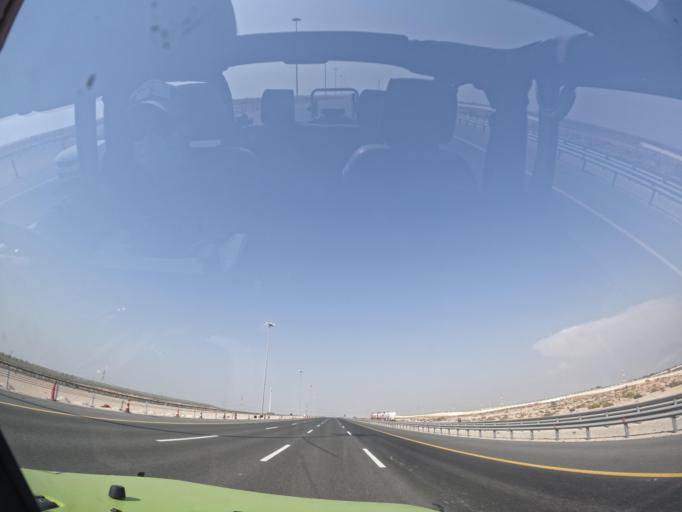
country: AE
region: Abu Dhabi
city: Abu Dhabi
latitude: 24.6385
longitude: 54.7835
